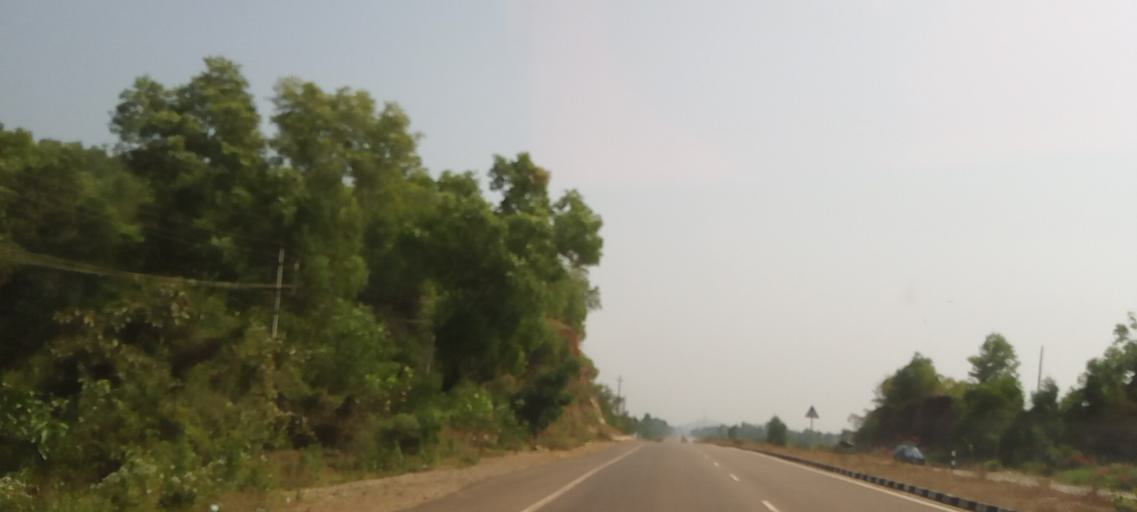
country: IN
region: Karnataka
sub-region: Uttar Kannada
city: Karwar
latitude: 14.9050
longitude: 74.0993
